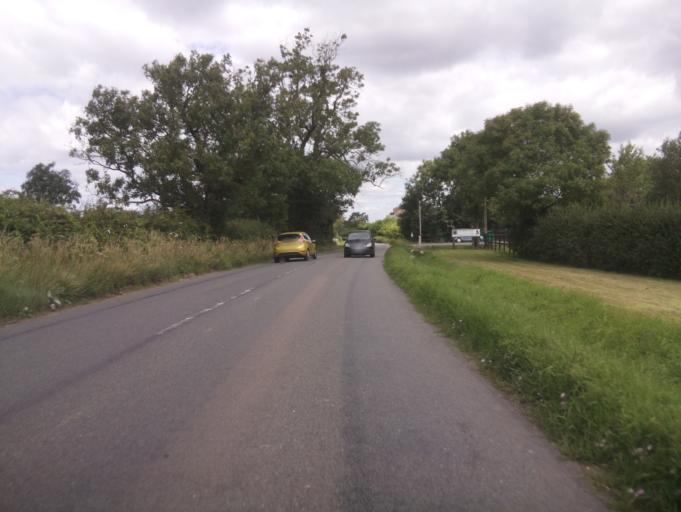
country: GB
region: England
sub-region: Buckinghamshire
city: Newton Longville
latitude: 51.9607
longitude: -0.8152
